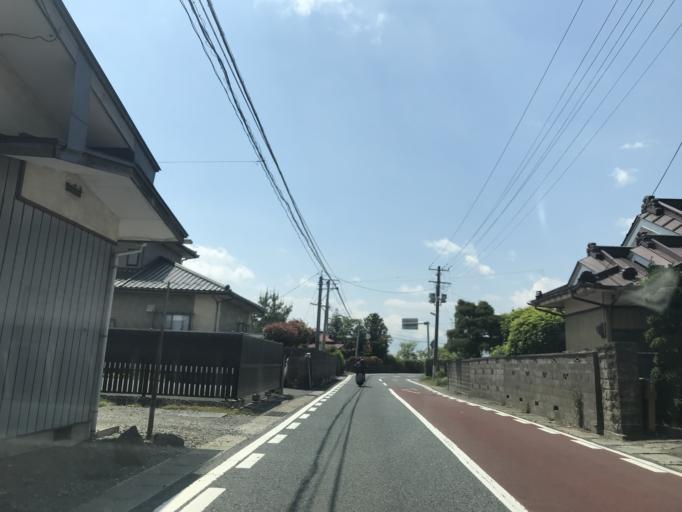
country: JP
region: Miyagi
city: Kogota
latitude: 38.5865
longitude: 141.0365
